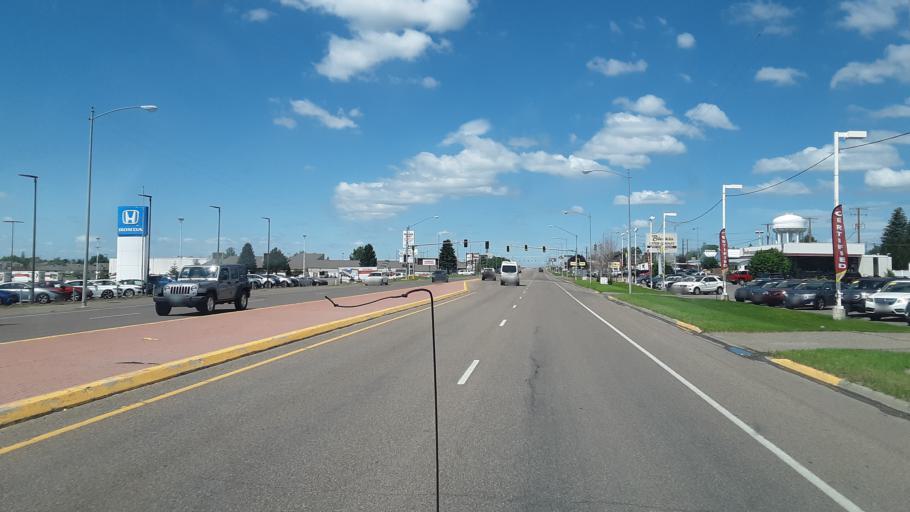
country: US
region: Montana
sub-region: Cascade County
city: Malmstrom Air Force Base
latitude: 47.4939
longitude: -111.2243
